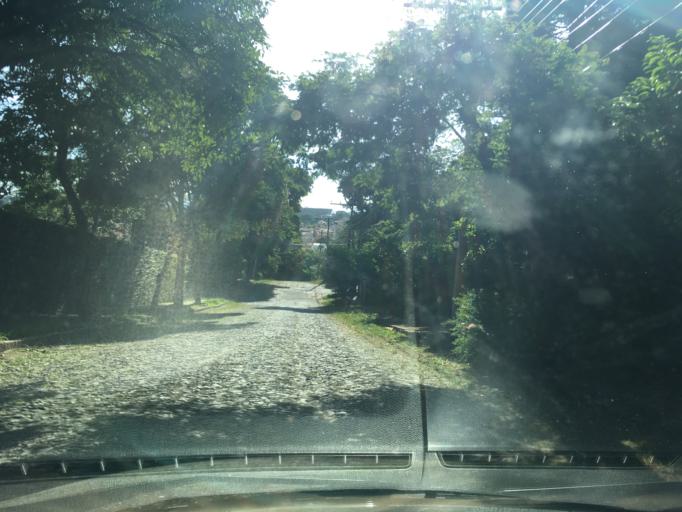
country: BR
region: Minas Gerais
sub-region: Belo Horizonte
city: Belo Horizonte
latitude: -19.8658
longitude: -43.9881
